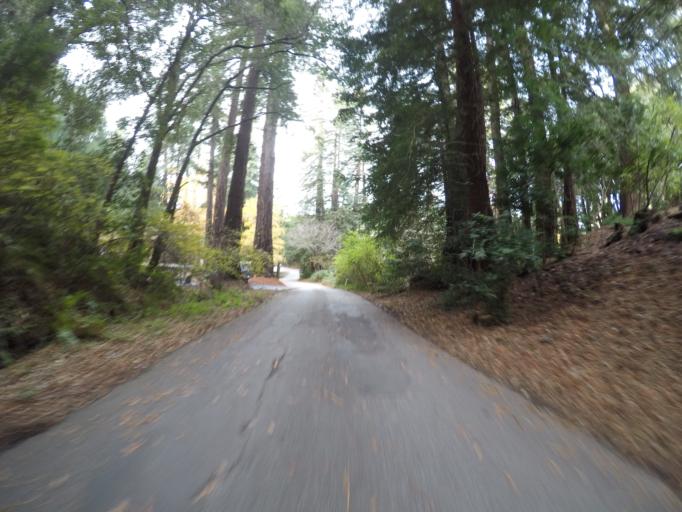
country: US
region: California
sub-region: Santa Cruz County
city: Scotts Valley
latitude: 37.0541
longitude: -122.0042
